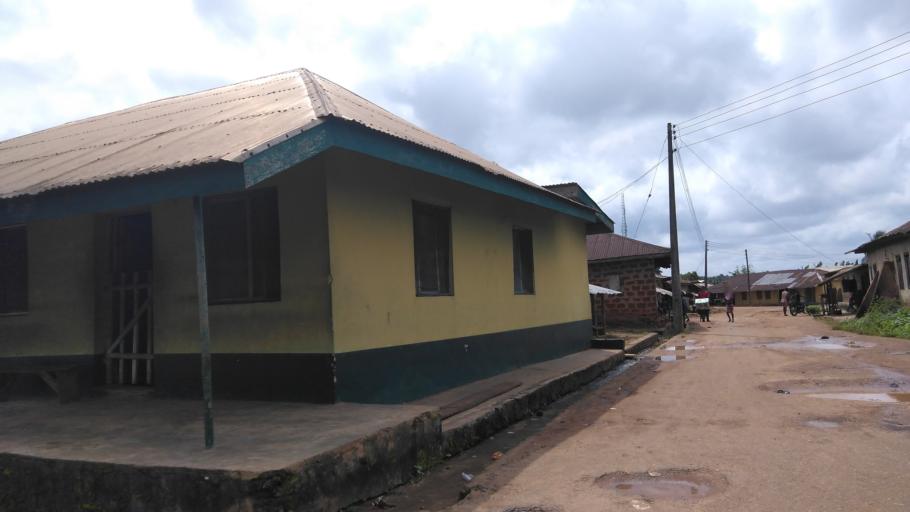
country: NG
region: Ogun
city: Abigi
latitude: 6.6004
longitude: 4.4953
